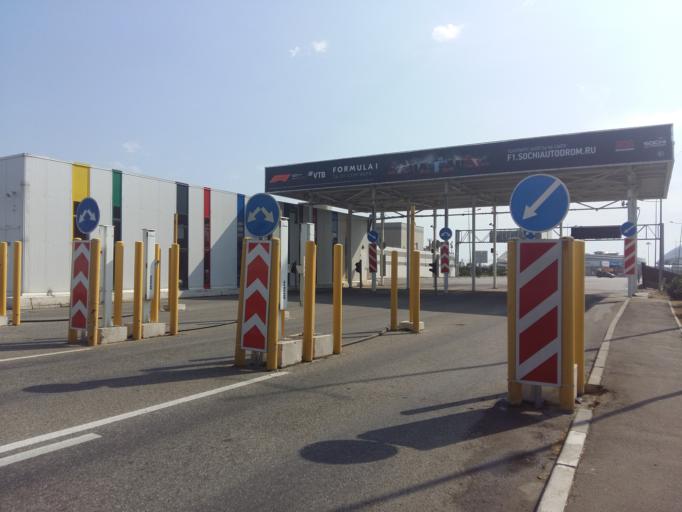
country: RU
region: Krasnodarskiy
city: Adler
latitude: 43.4107
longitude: 39.9658
